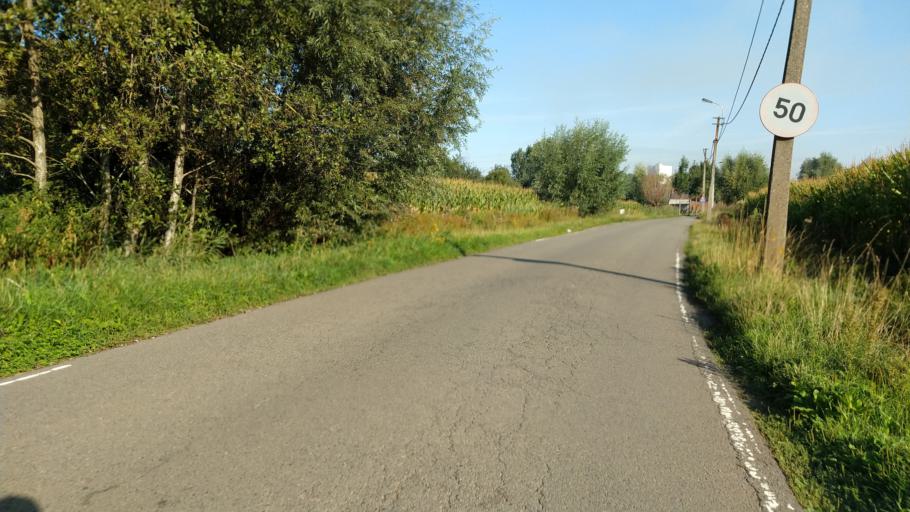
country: BE
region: Flanders
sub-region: Provincie Oost-Vlaanderen
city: Zelzate
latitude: 51.1453
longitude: 3.8128
